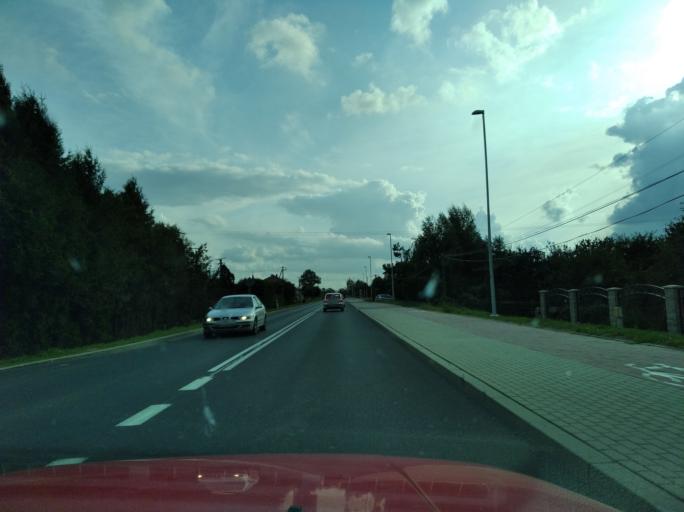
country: PL
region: Subcarpathian Voivodeship
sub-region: Powiat jaroslawski
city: Pawlosiow
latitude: 49.9948
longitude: 22.6658
